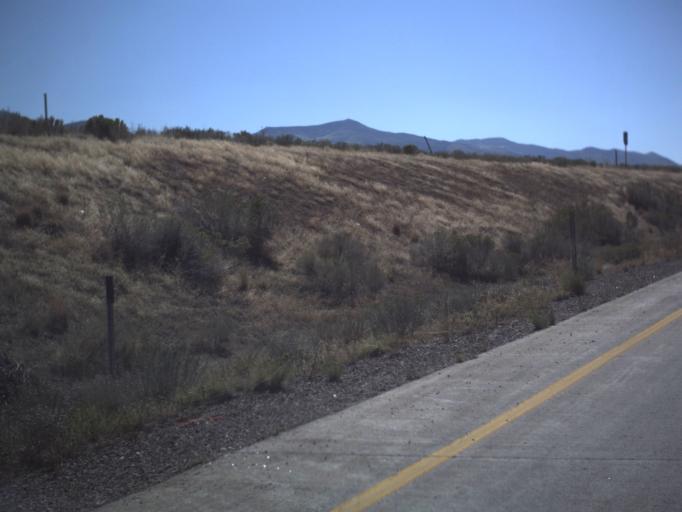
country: US
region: Utah
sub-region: Sevier County
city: Richfield
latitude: 38.7490
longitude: -112.1069
